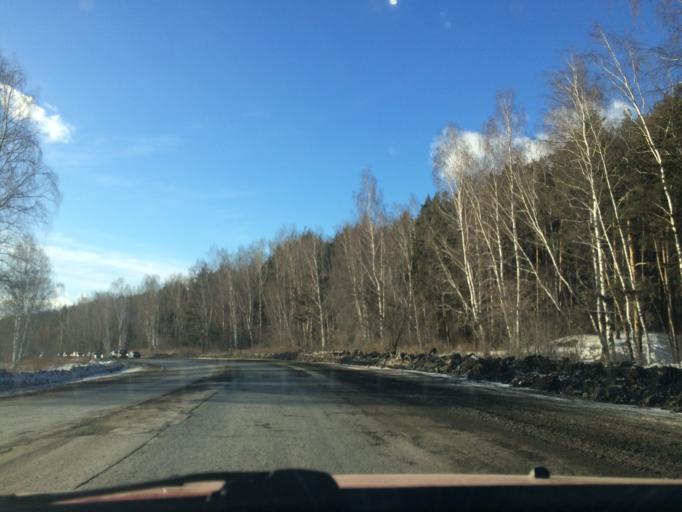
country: RU
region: Sverdlovsk
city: Istok
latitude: 56.7868
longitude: 60.7583
